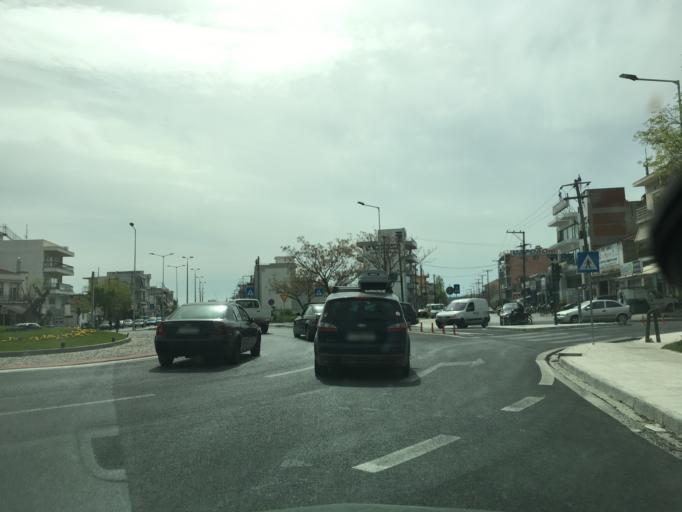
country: GR
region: Thessaly
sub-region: Nomos Magnisias
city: Nea Ionia
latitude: 39.3669
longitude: 22.9227
